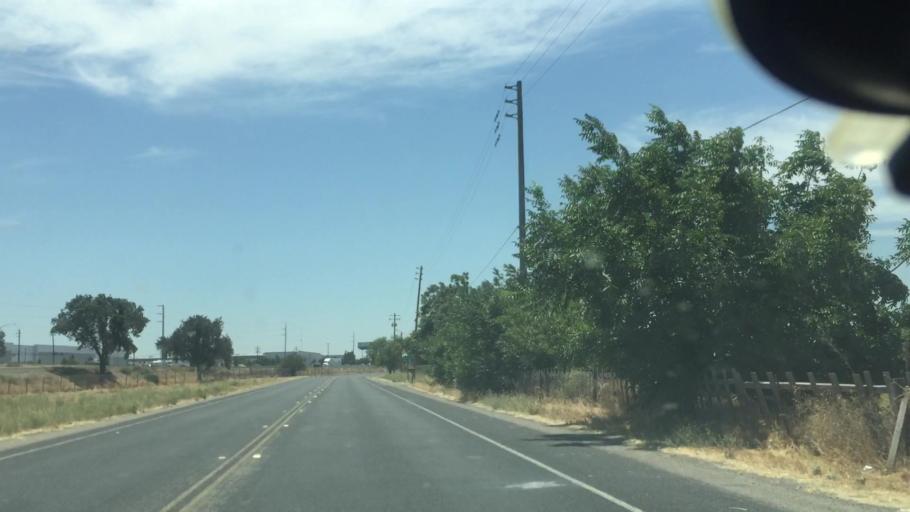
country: US
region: California
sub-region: San Joaquin County
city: French Camp
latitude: 37.8545
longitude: -121.2836
